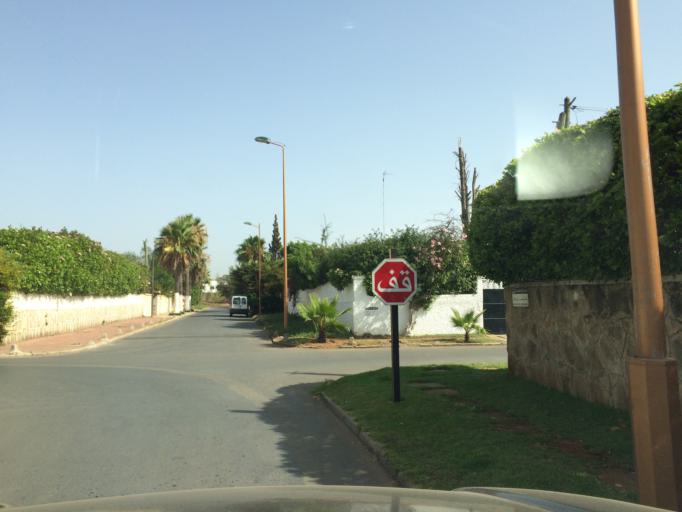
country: MA
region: Rabat-Sale-Zemmour-Zaer
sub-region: Rabat
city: Rabat
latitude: 33.9886
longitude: -6.8330
